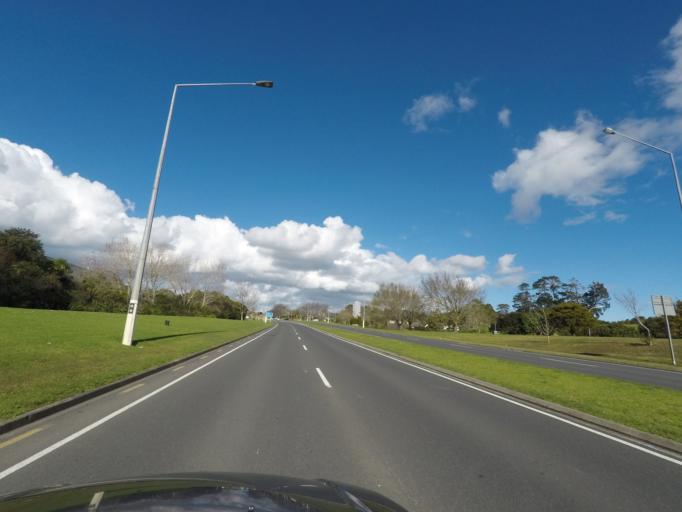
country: NZ
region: Auckland
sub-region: Auckland
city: Rothesay Bay
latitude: -36.7321
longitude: 174.7054
